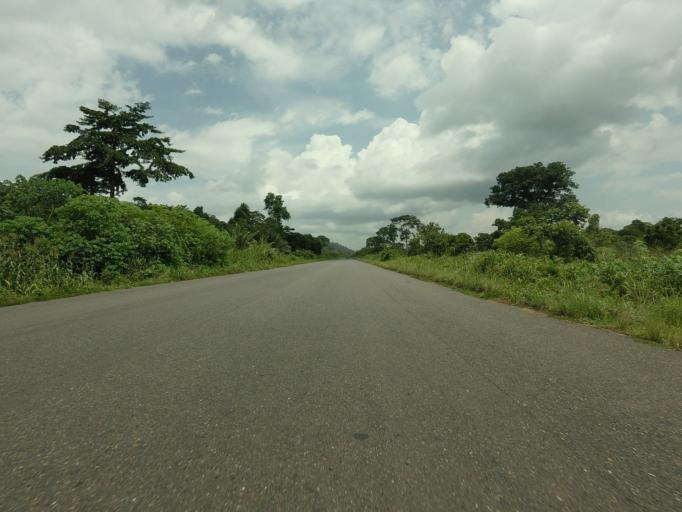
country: GH
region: Volta
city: Ho
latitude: 6.4914
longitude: 0.2009
